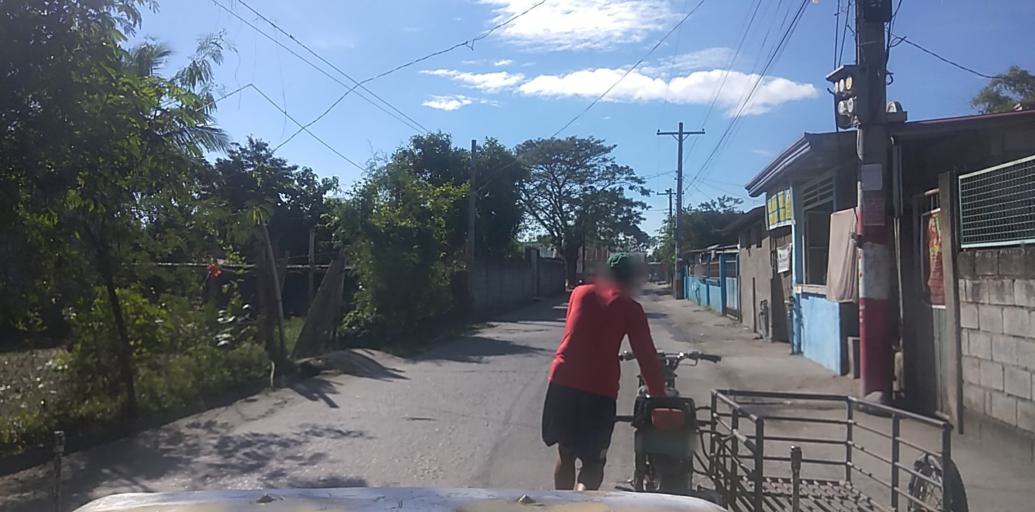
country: PH
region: Central Luzon
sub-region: Province of Pampanga
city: San Patricio
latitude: 15.0986
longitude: 120.7137
